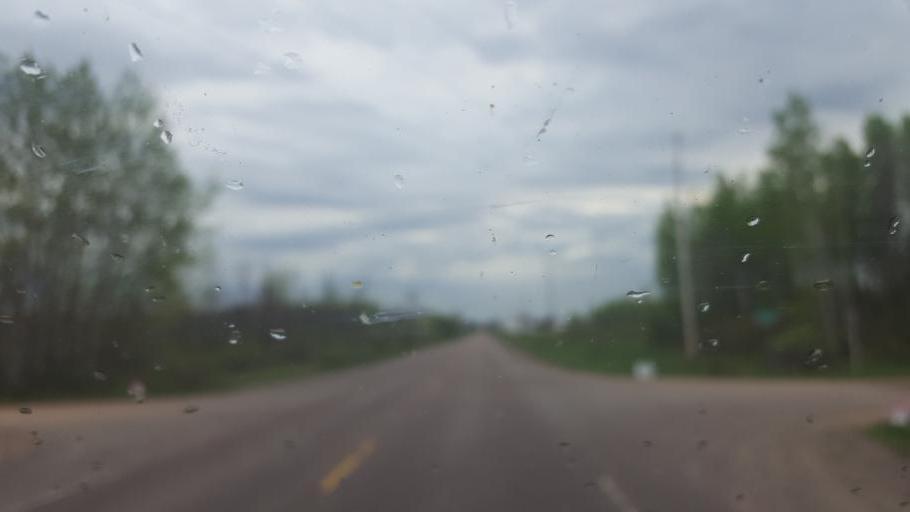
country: US
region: Wisconsin
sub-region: Marathon County
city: Spencer
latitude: 44.6416
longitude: -90.3569
